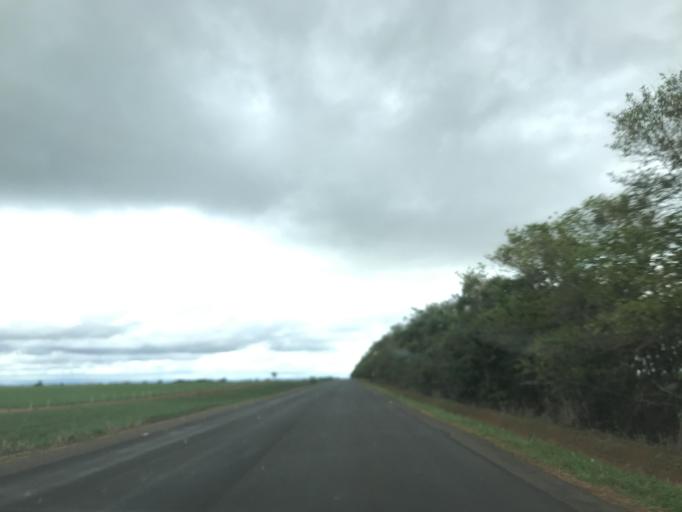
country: BR
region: Goias
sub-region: Vianopolis
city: Vianopolis
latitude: -16.7983
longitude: -48.5200
